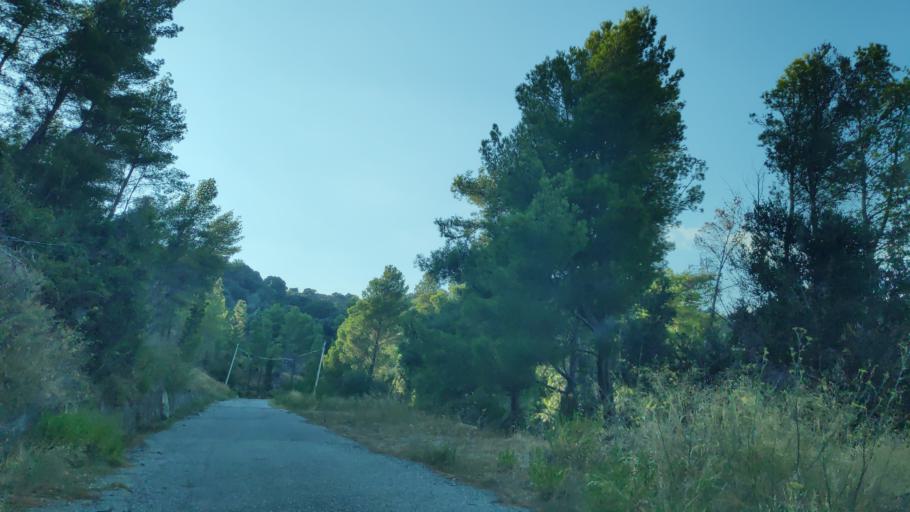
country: IT
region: Calabria
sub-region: Provincia di Reggio Calabria
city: Placanica
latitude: 38.4101
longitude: 16.4314
